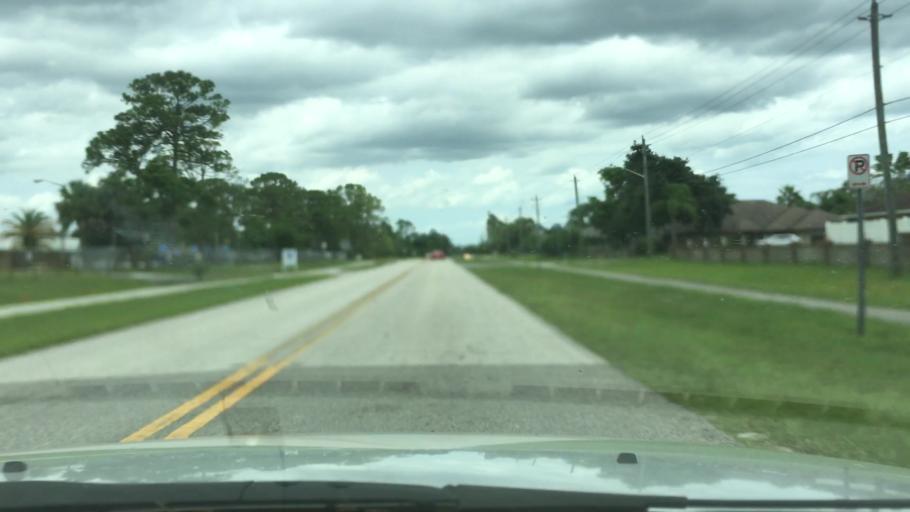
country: US
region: Florida
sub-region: Volusia County
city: Holly Hill
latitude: 29.2233
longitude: -81.0704
